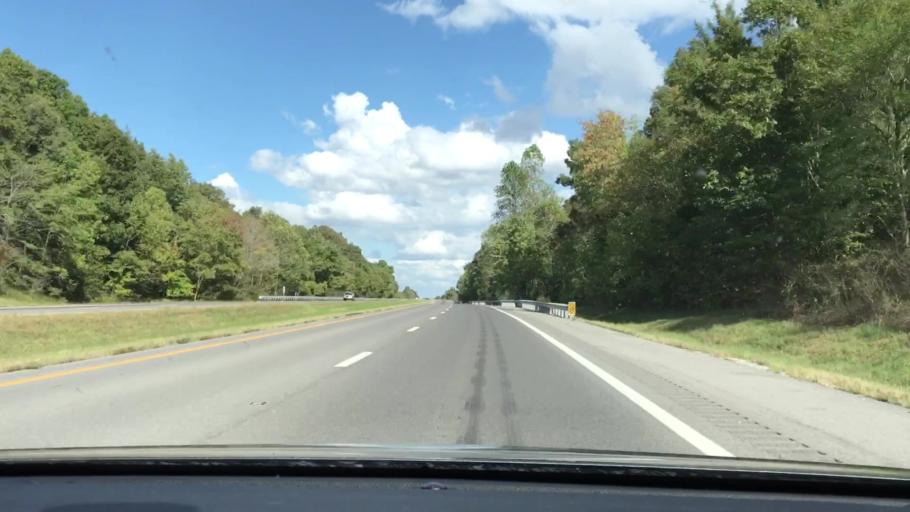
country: US
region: Kentucky
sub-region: Graves County
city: Mayfield
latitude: 36.7916
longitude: -88.5181
